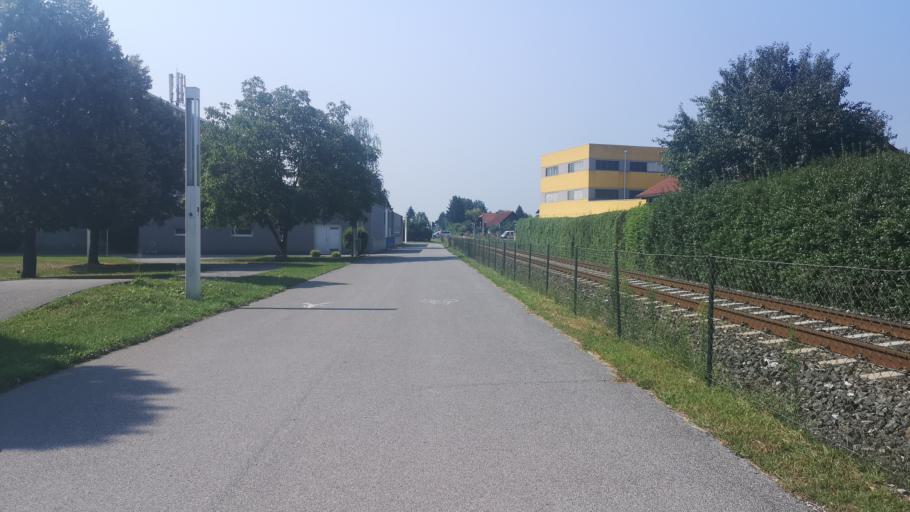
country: AT
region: Styria
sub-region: Politischer Bezirk Graz-Umgebung
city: Seiersberg
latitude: 47.0113
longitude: 15.4031
